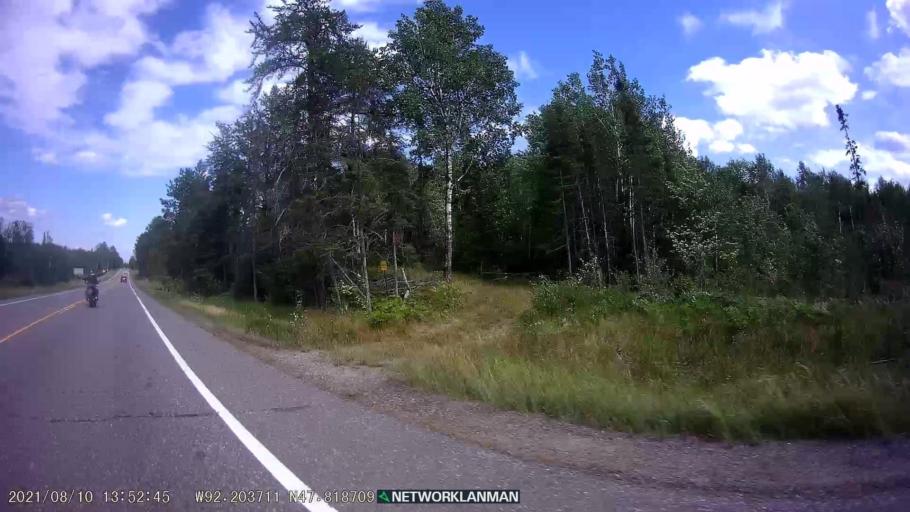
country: US
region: Minnesota
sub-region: Saint Louis County
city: Babbitt
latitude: 47.8188
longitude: -92.2036
